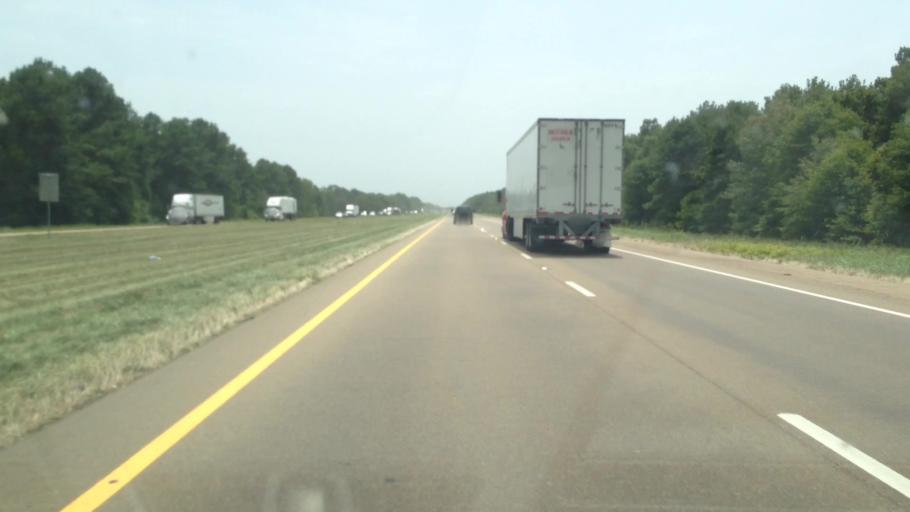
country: US
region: Texas
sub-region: Morris County
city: Naples
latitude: 33.3443
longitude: -94.6584
